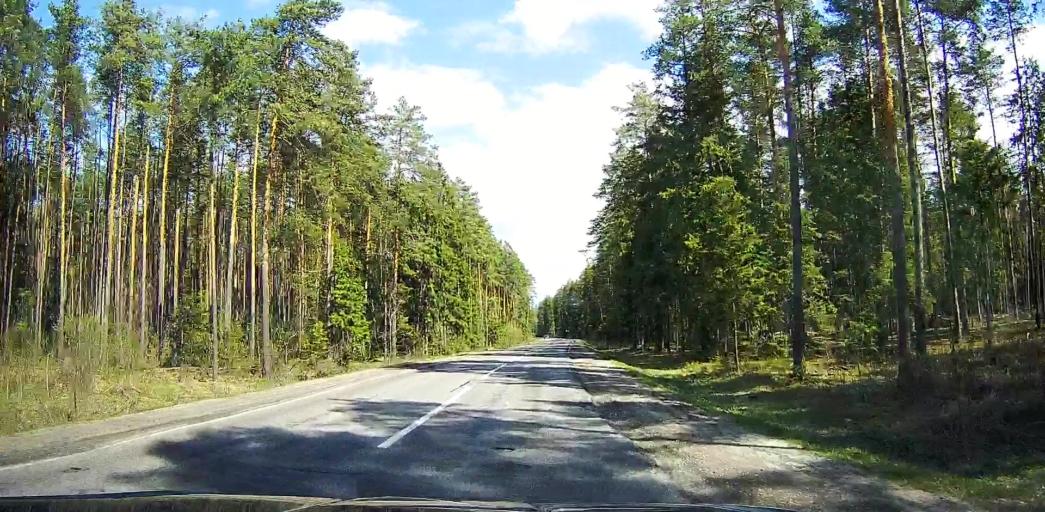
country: RU
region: Moskovskaya
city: Davydovo
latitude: 55.5596
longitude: 38.8414
